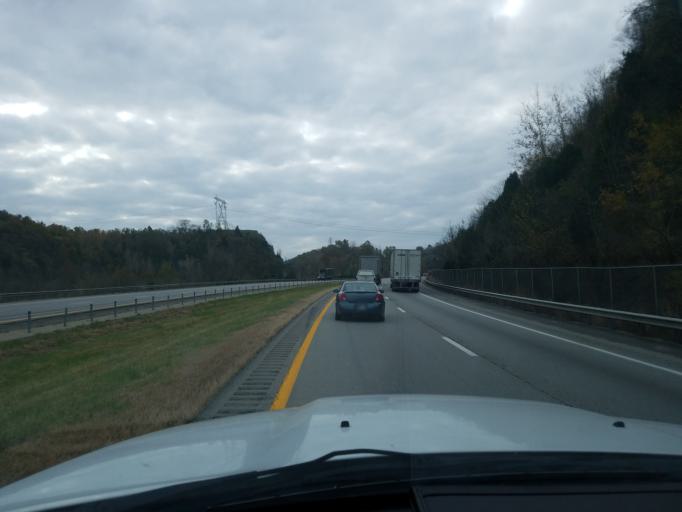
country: US
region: Kentucky
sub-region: Trimble County
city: Providence
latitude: 38.5978
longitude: -85.1733
